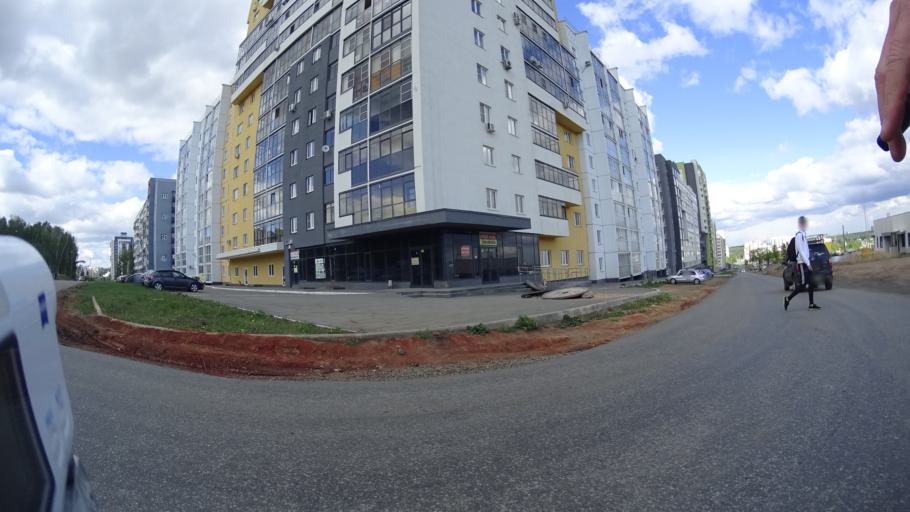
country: RU
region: Chelyabinsk
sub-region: Gorod Chelyabinsk
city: Chelyabinsk
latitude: 55.1599
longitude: 61.2858
